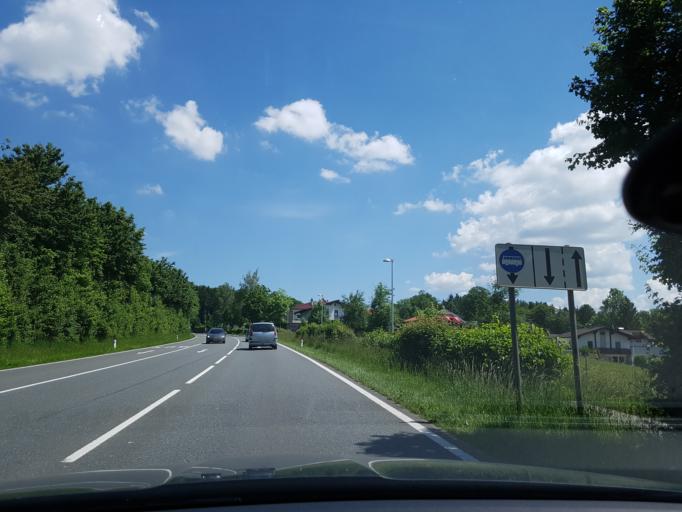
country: AT
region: Salzburg
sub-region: Politischer Bezirk Salzburg-Umgebung
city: Elixhausen
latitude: 47.8532
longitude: 13.0547
